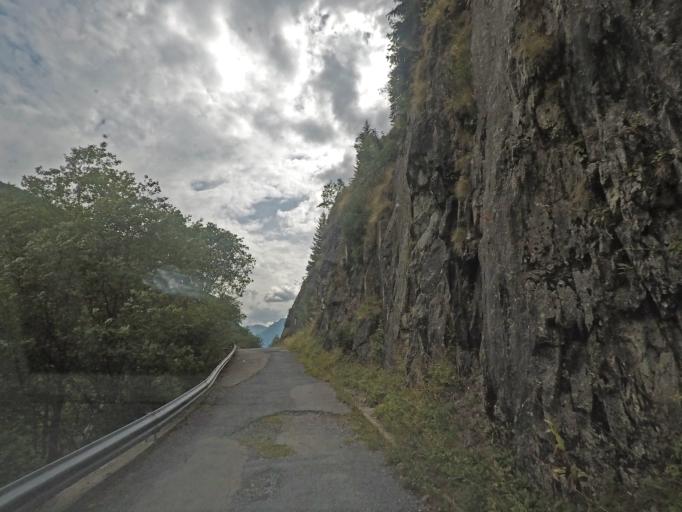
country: CH
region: Valais
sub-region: Brig District
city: Naters
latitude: 46.3707
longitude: 8.0001
